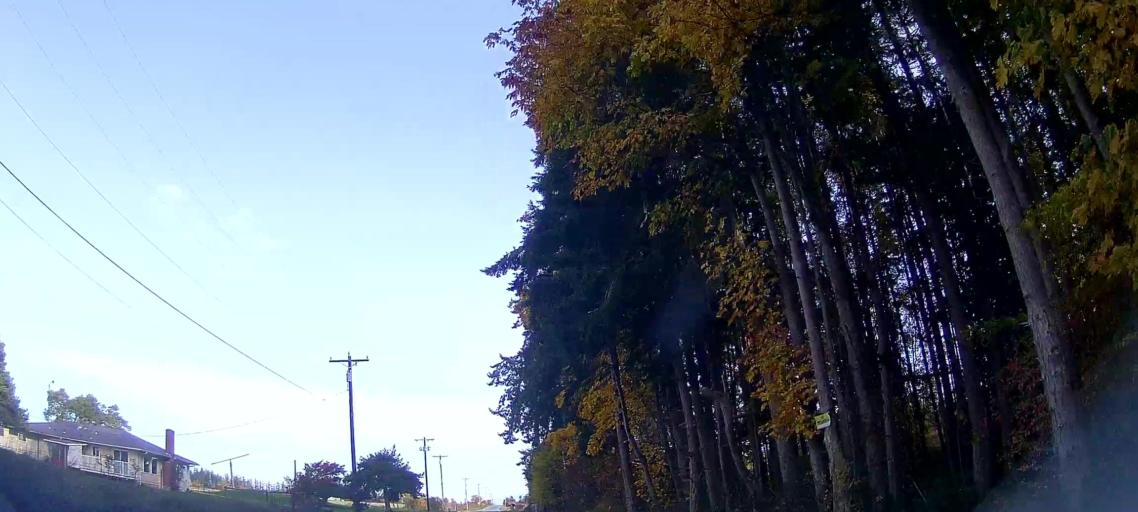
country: US
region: Washington
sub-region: Snohomish County
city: Stanwood
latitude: 48.2545
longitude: -122.4516
